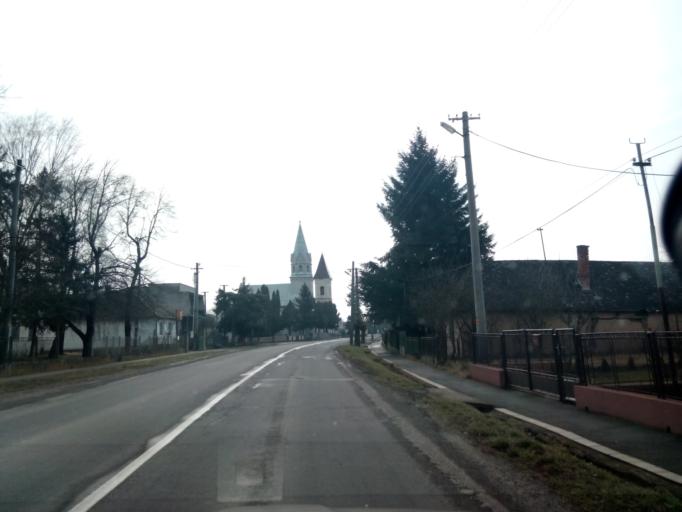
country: SK
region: Kosicky
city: Trebisov
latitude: 48.6036
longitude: 21.6271
